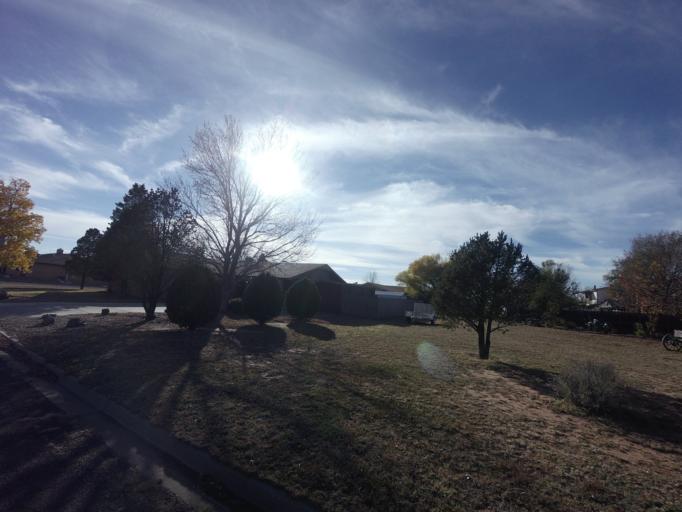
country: US
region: New Mexico
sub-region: Curry County
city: Clovis
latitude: 34.4153
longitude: -103.1764
